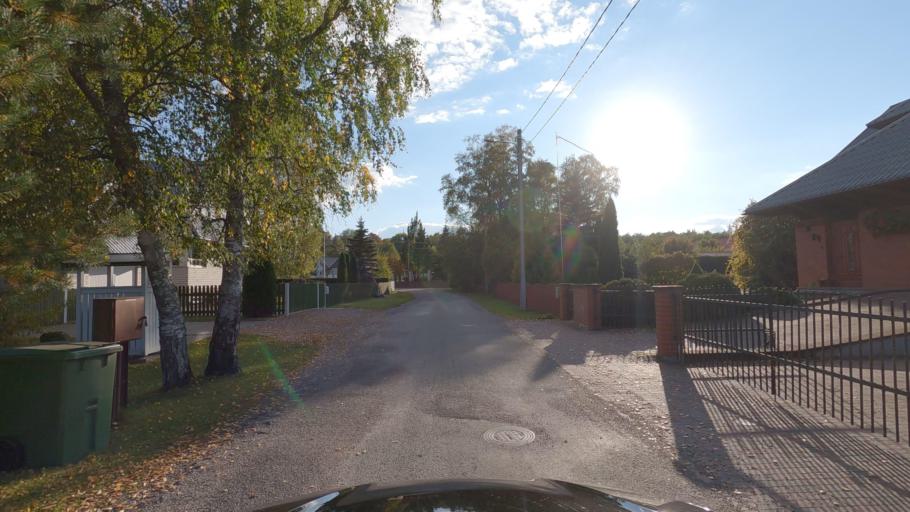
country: EE
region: Harju
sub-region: Saku vald
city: Saku
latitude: 59.3019
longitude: 24.6512
